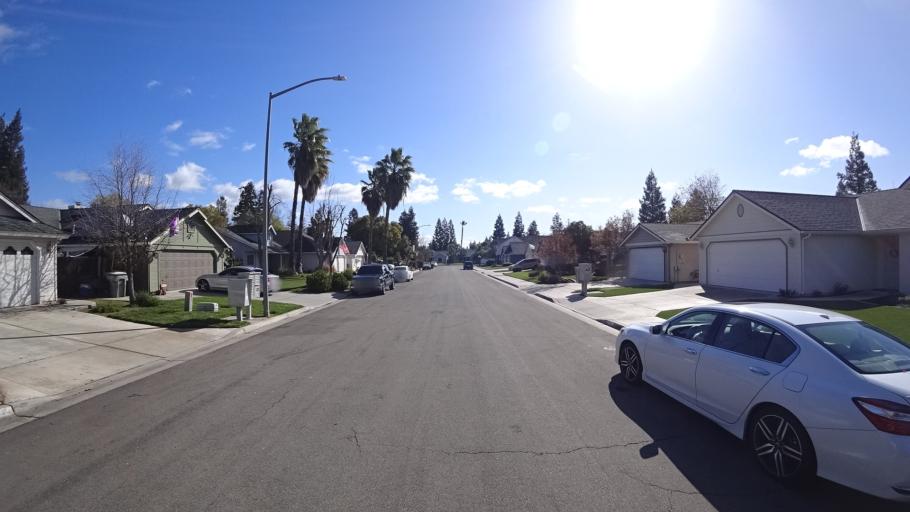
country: US
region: California
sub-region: Fresno County
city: West Park
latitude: 36.8231
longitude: -119.8794
